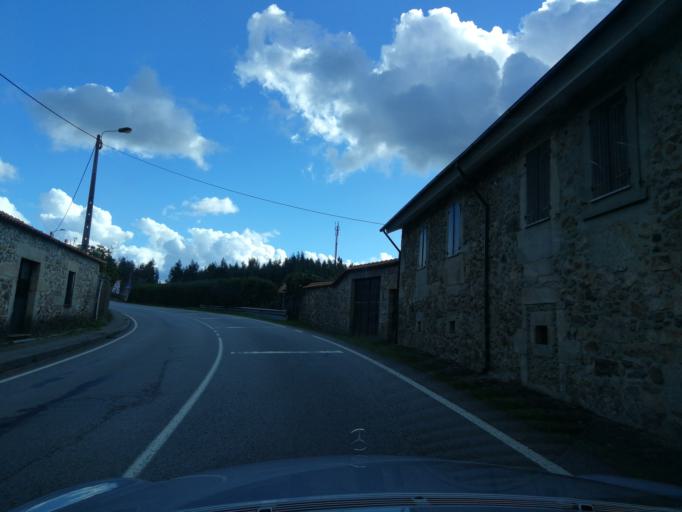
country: PT
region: Braga
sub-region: Vila Verde
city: Prado
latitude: 41.6628
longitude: -8.5202
